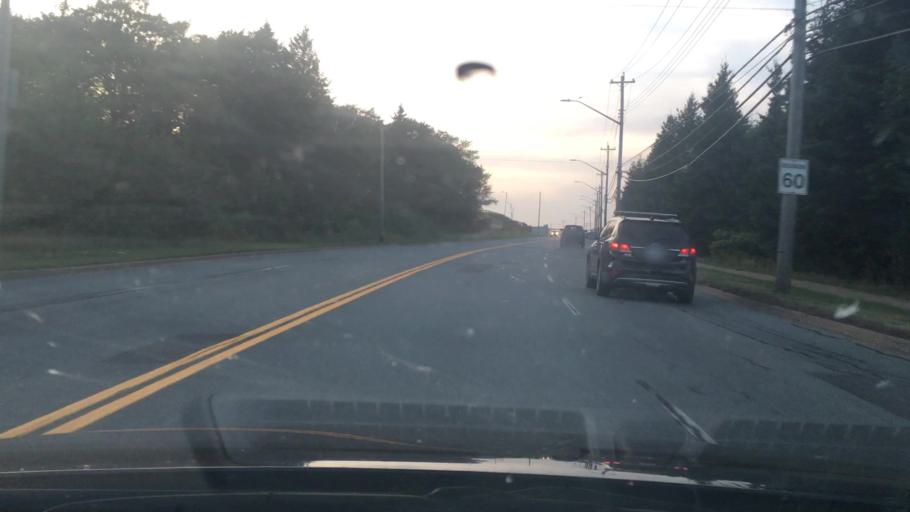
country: CA
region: Nova Scotia
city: Halifax
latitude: 44.6373
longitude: -63.5290
